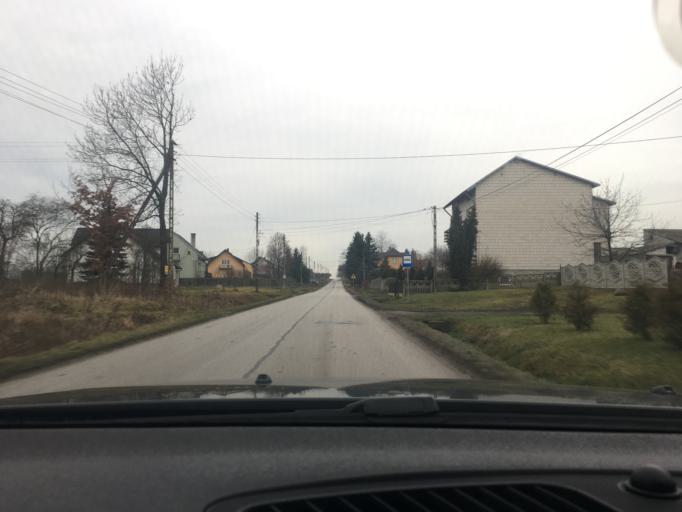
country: PL
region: Swietokrzyskie
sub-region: Powiat jedrzejowski
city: Jedrzejow
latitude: 50.6408
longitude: 20.3552
